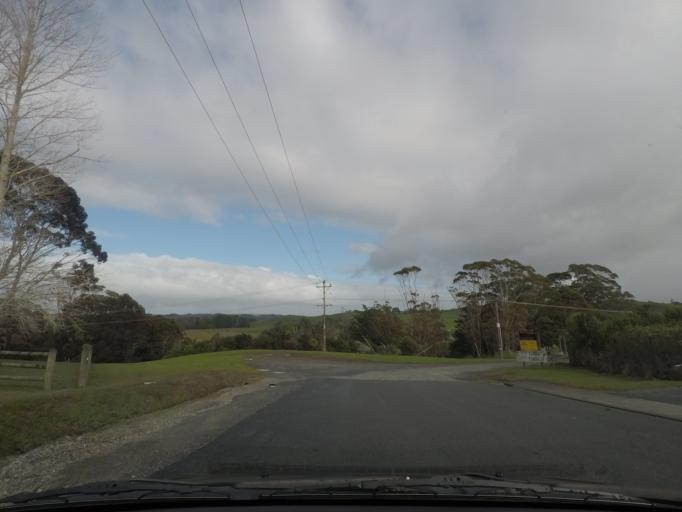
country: NZ
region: Auckland
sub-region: Auckland
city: Warkworth
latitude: -36.4210
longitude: 174.7213
